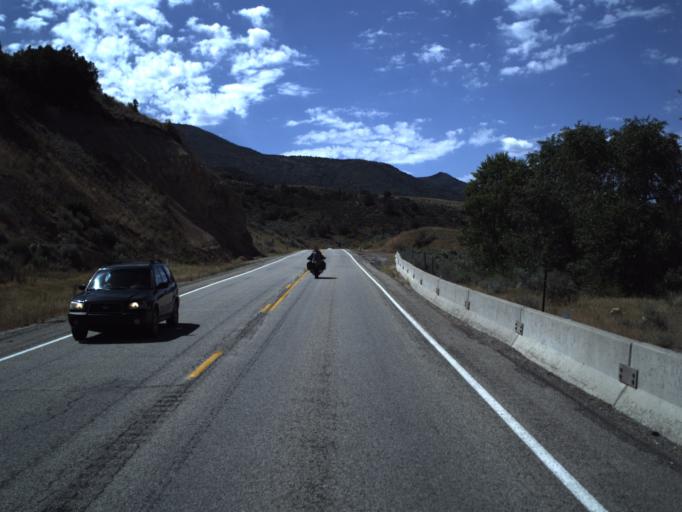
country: US
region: Utah
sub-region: Utah County
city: Woodland Hills
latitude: 39.9782
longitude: -111.5033
